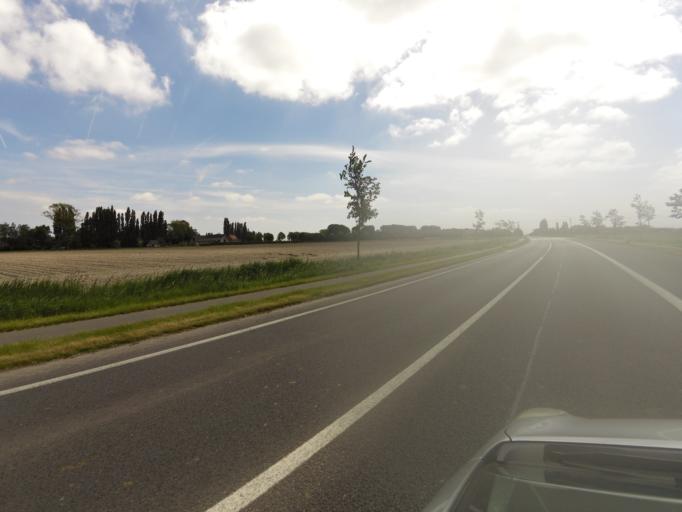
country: BE
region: Flanders
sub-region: Provincie West-Vlaanderen
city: Diksmuide
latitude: 51.0767
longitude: 2.8745
